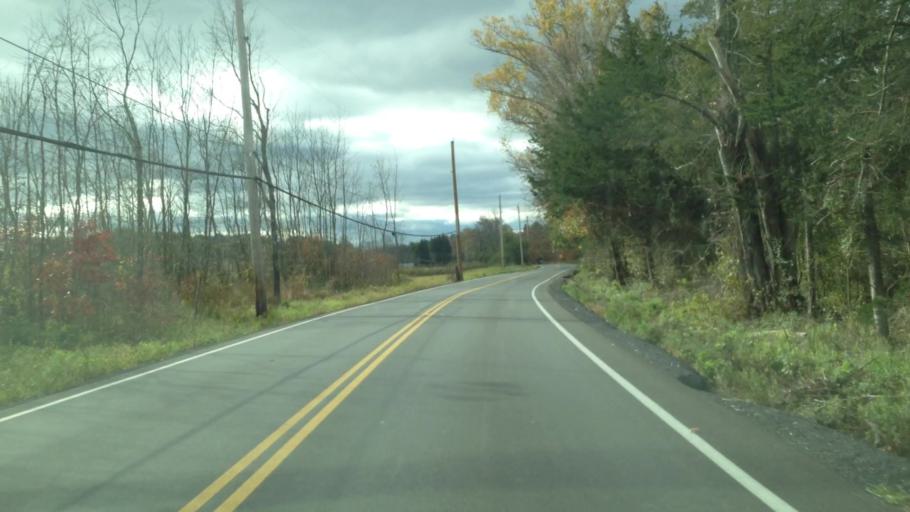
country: US
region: New York
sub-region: Ulster County
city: New Paltz
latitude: 41.7641
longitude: -74.0957
